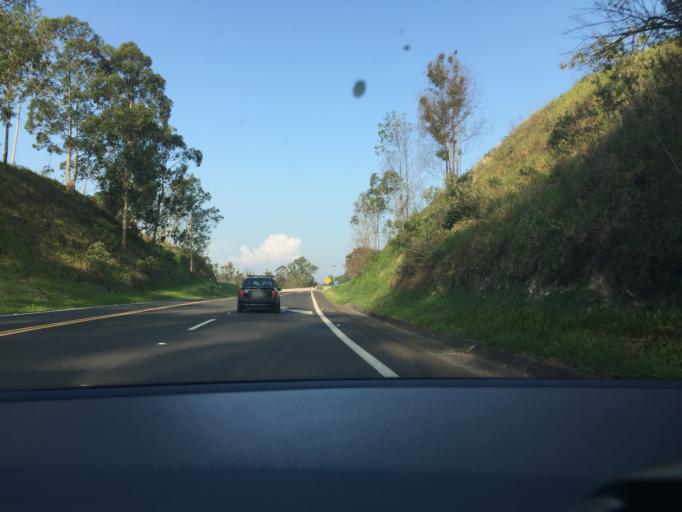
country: BR
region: Sao Paulo
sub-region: Louveira
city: Louveira
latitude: -23.0713
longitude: -46.9044
